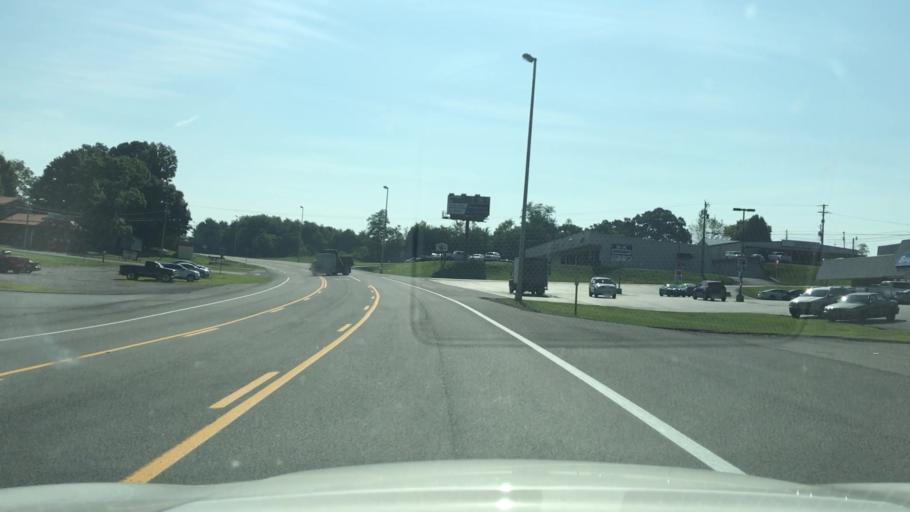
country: US
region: Tennessee
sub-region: Pickett County
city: Byrdstown
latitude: 36.5729
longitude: -85.1477
